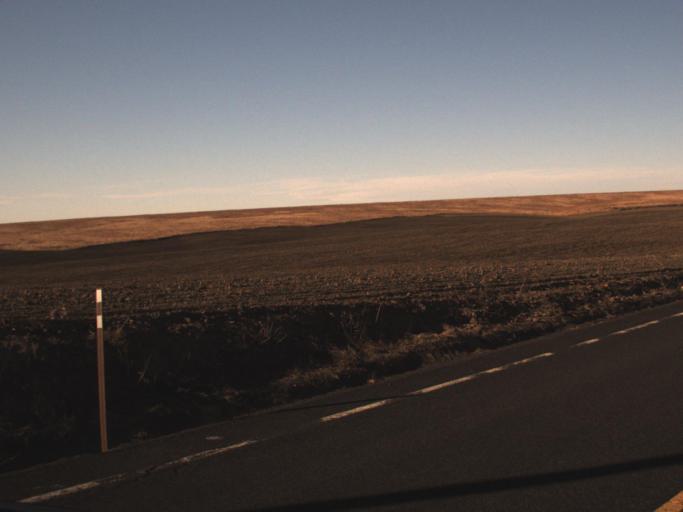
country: US
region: Washington
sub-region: Adams County
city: Ritzville
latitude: 47.0171
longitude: -118.3506
